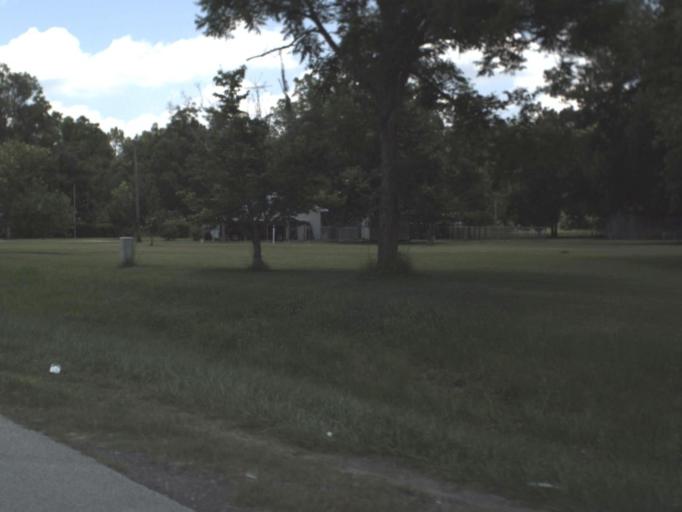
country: US
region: Florida
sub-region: Bradford County
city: Starke
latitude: 30.0103
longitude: -82.1420
